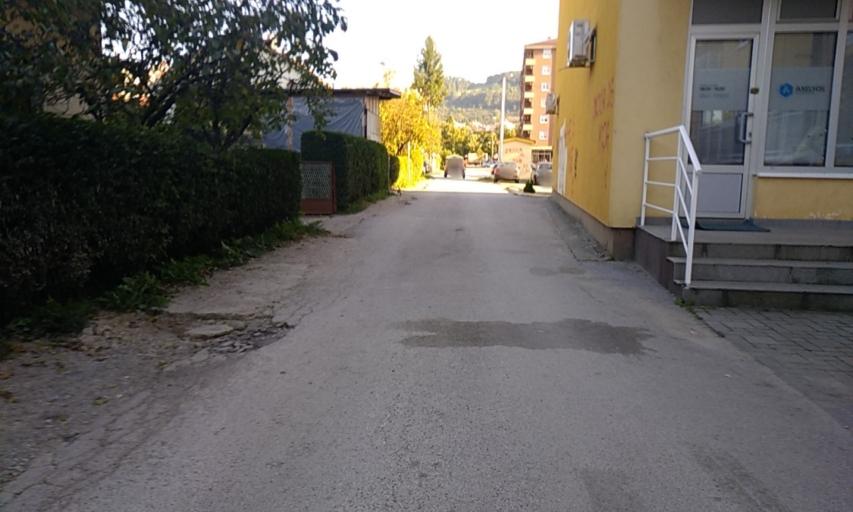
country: BA
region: Republika Srpska
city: Starcevica
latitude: 44.7651
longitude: 17.2038
